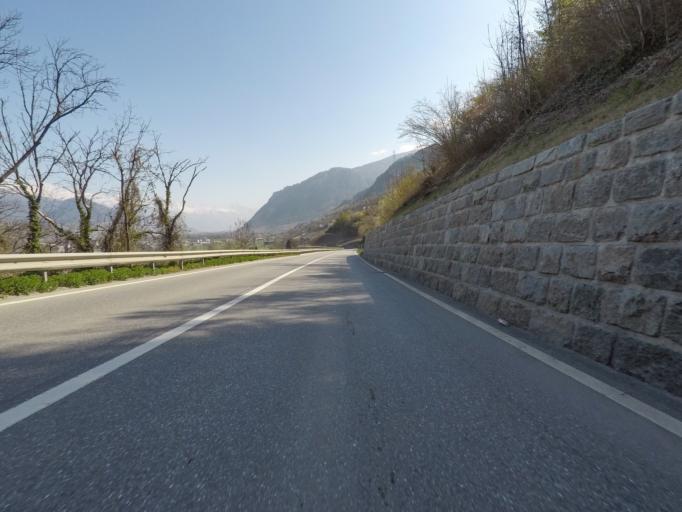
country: CH
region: Valais
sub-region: Sion District
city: Sitten
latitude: 46.2202
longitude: 7.3677
